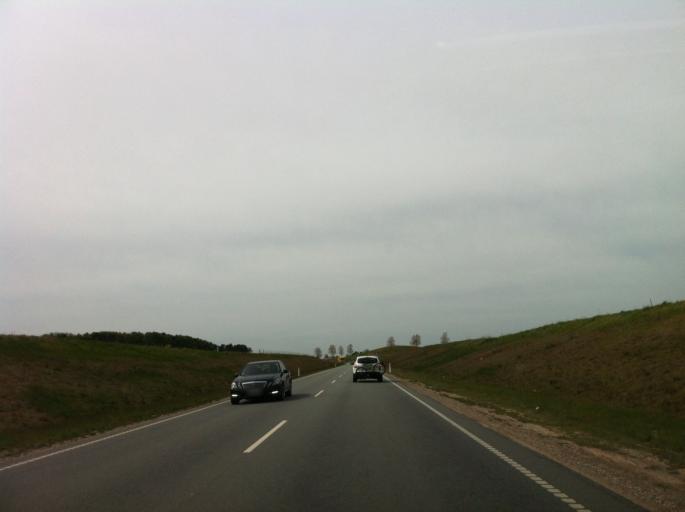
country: DK
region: Capital Region
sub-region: Frederikssund Kommune
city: Slangerup
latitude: 55.8796
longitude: 12.2022
